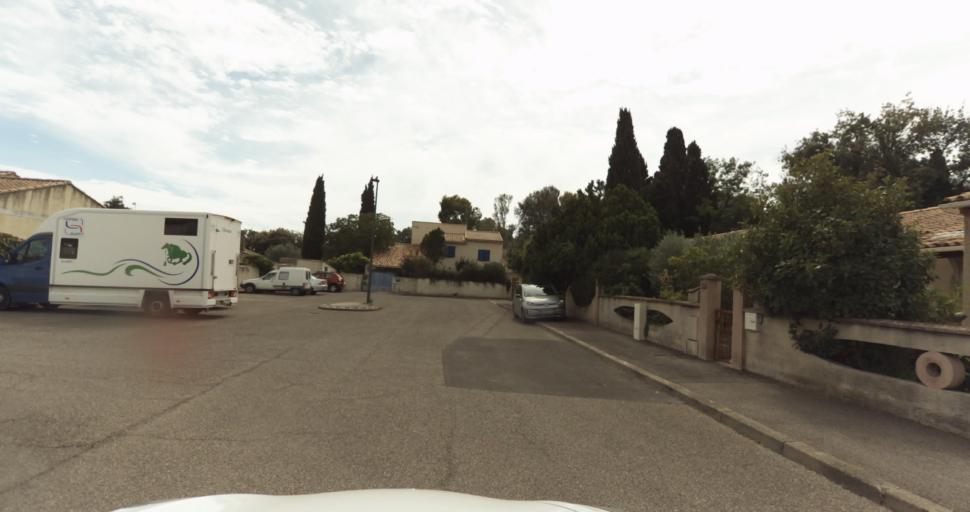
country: FR
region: Provence-Alpes-Cote d'Azur
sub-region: Departement des Bouches-du-Rhone
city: Miramas
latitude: 43.5771
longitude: 4.9921
